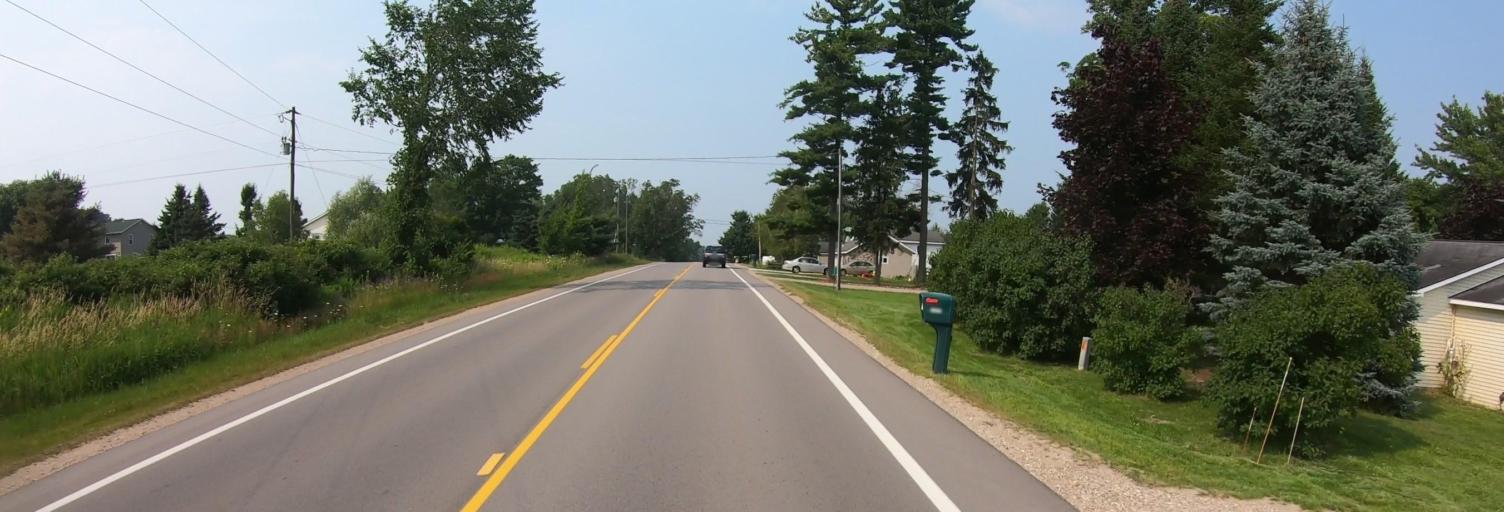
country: US
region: Michigan
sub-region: Charlevoix County
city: Charlevoix
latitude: 45.2241
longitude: -85.2613
